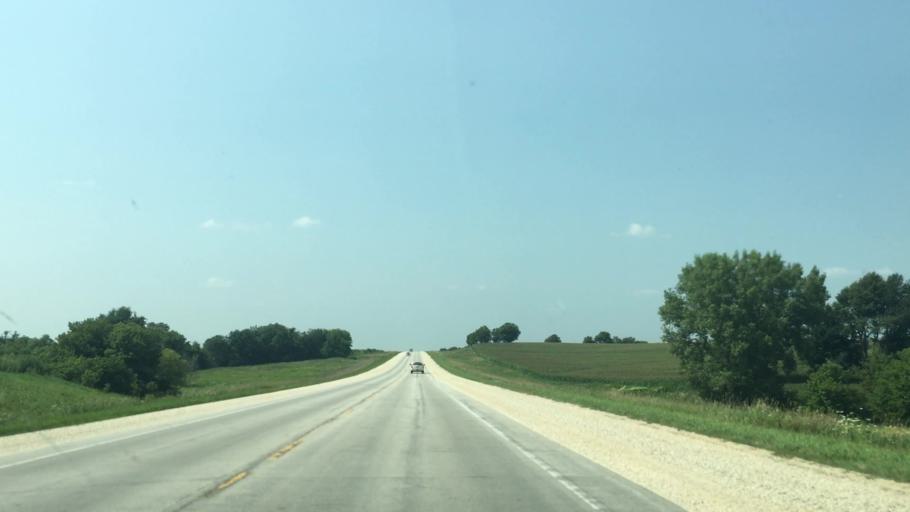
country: US
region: Iowa
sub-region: Winneshiek County
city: Decorah
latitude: 43.3771
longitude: -91.8163
